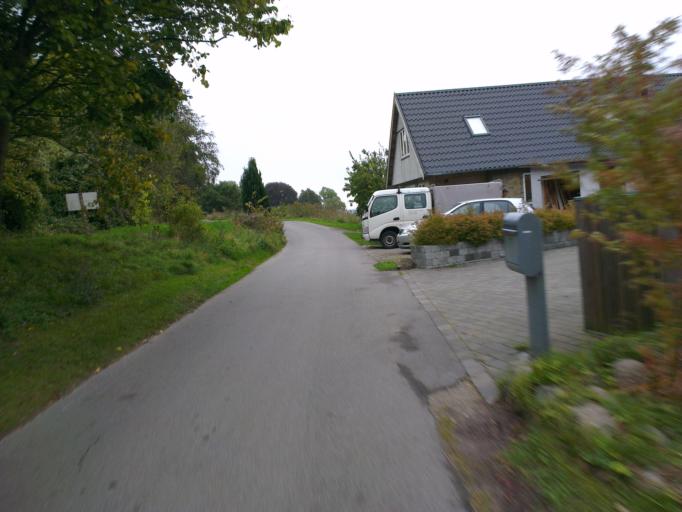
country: DK
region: Capital Region
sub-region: Frederikssund Kommune
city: Frederikssund
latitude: 55.8345
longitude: 12.0324
